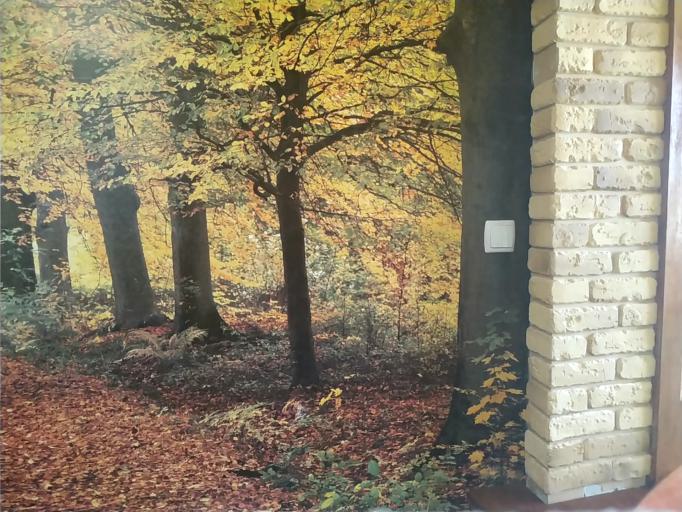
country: RU
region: Tverskaya
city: Krasnomayskiy
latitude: 57.7172
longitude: 34.4765
